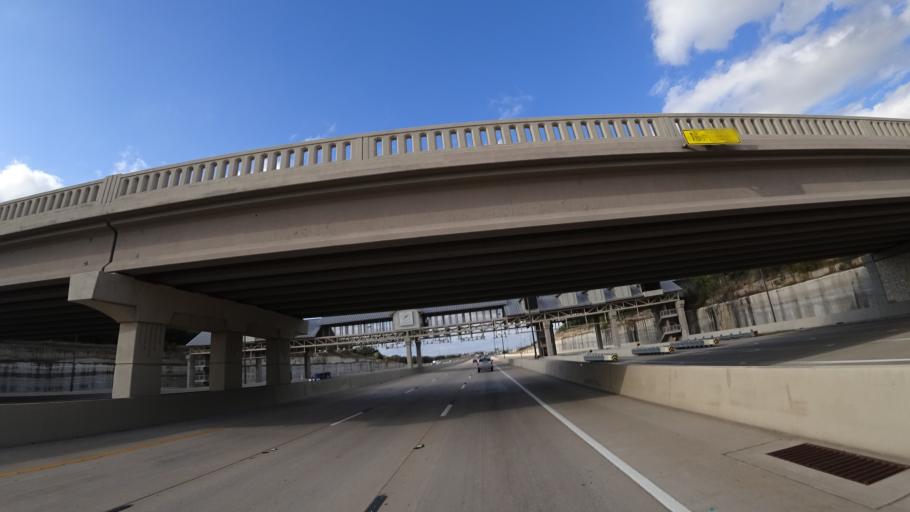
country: US
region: Texas
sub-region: Williamson County
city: Cedar Park
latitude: 30.5137
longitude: -97.8128
